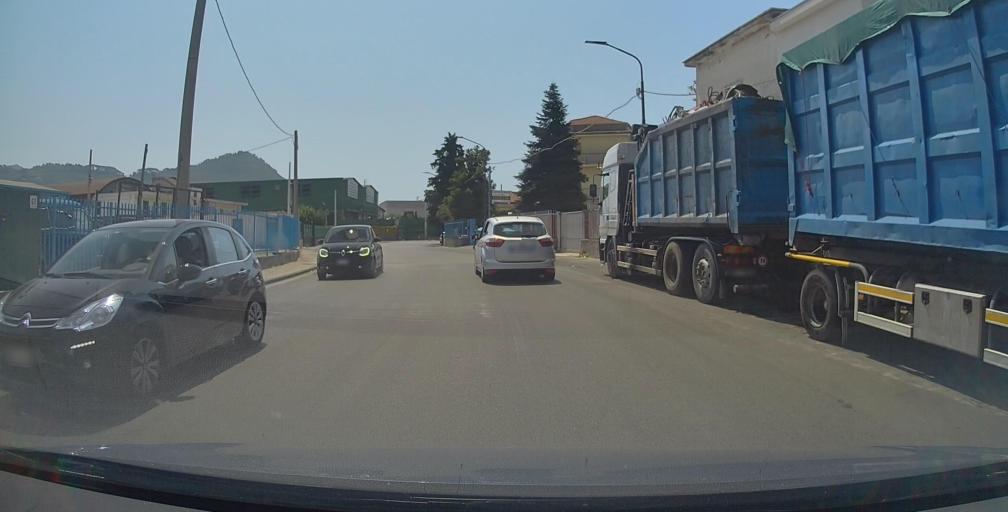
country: IT
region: Campania
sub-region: Provincia di Salerno
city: Cava De Tirreni
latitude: 40.7172
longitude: 14.6958
